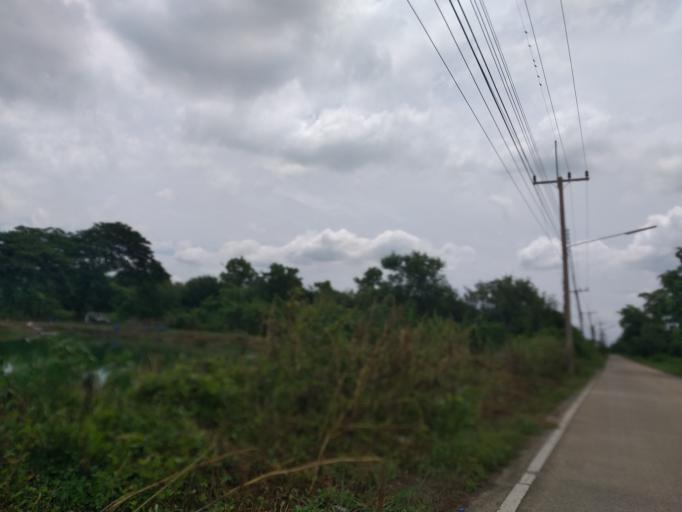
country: TH
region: Pathum Thani
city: Ban Lam Luk Ka
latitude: 13.9637
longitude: 100.8540
